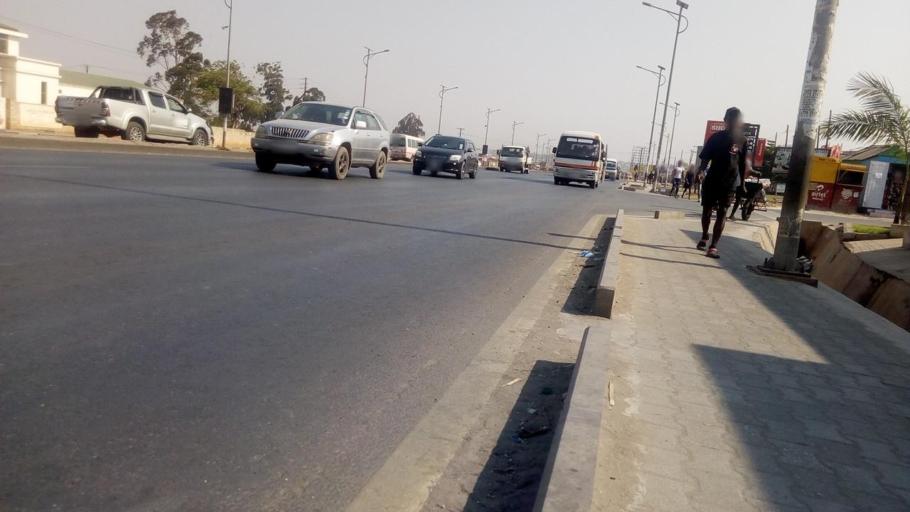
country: ZM
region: Lusaka
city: Lusaka
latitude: -15.3630
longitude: 28.2767
